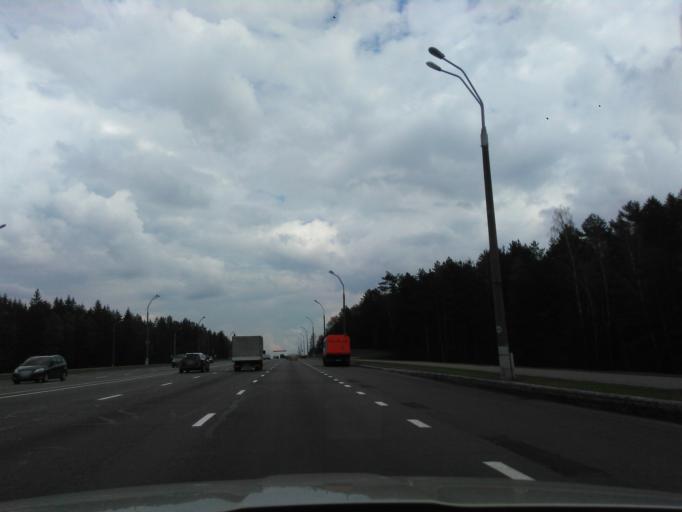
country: BY
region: Minsk
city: Lyeskawka
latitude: 53.9581
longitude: 27.7262
